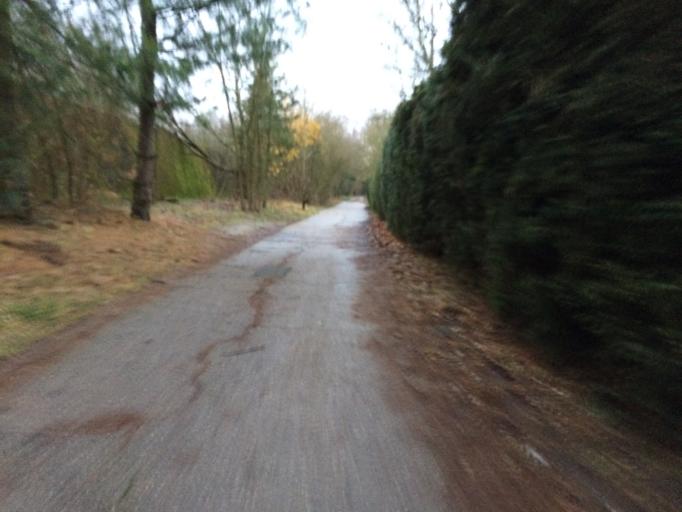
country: FR
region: Ile-de-France
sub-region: Departement de l'Essonne
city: Verrieres-le-Buisson
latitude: 48.7509
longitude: 2.2812
